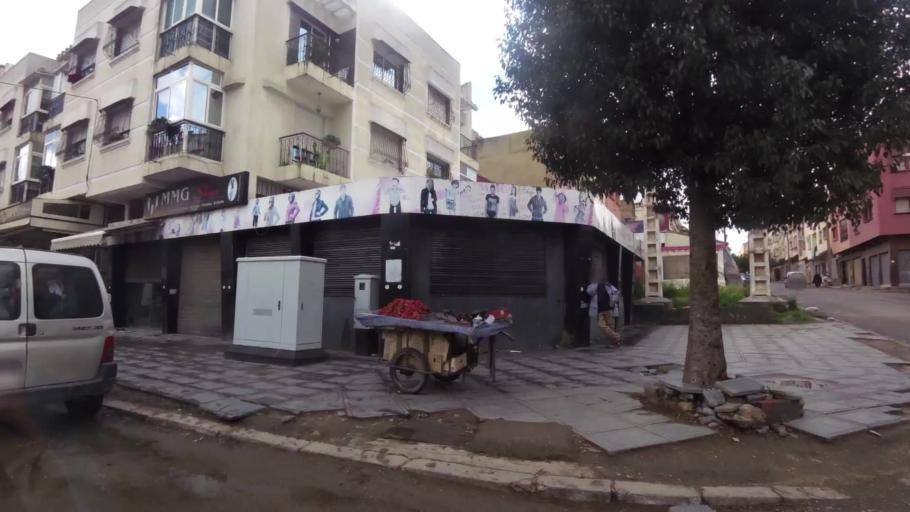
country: MA
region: Grand Casablanca
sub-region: Nouaceur
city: Bouskoura
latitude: 33.5147
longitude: -7.6480
